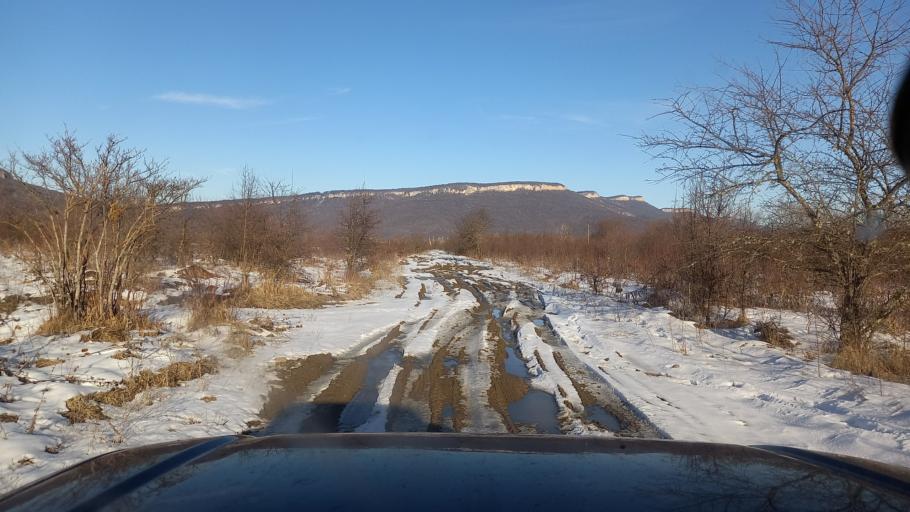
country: RU
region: Adygeya
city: Kamennomostskiy
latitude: 44.2120
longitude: 40.1666
